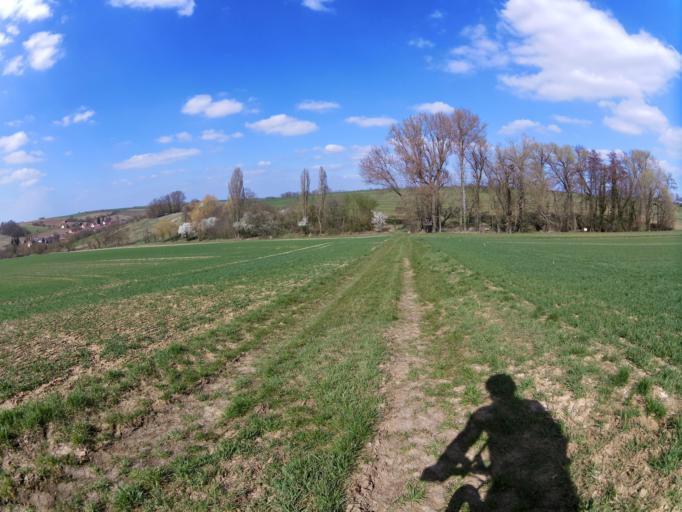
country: DE
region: Bavaria
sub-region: Regierungsbezirk Unterfranken
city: Dettelbach
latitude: 49.8371
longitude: 10.1542
